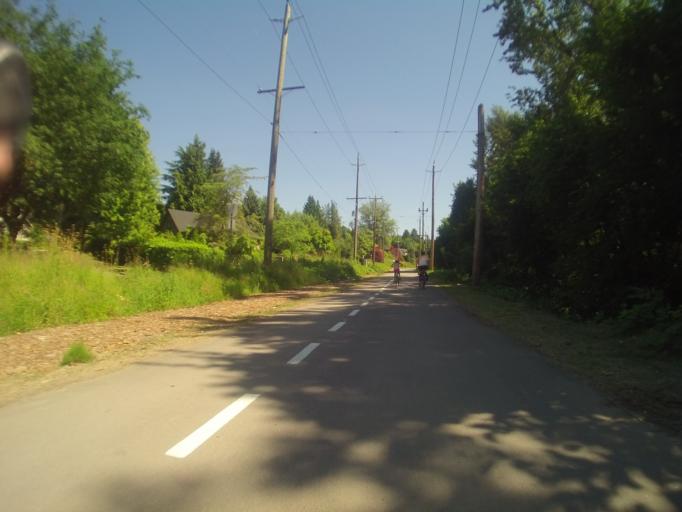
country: CA
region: British Columbia
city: Vancouver
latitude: 49.2448
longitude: -123.1481
